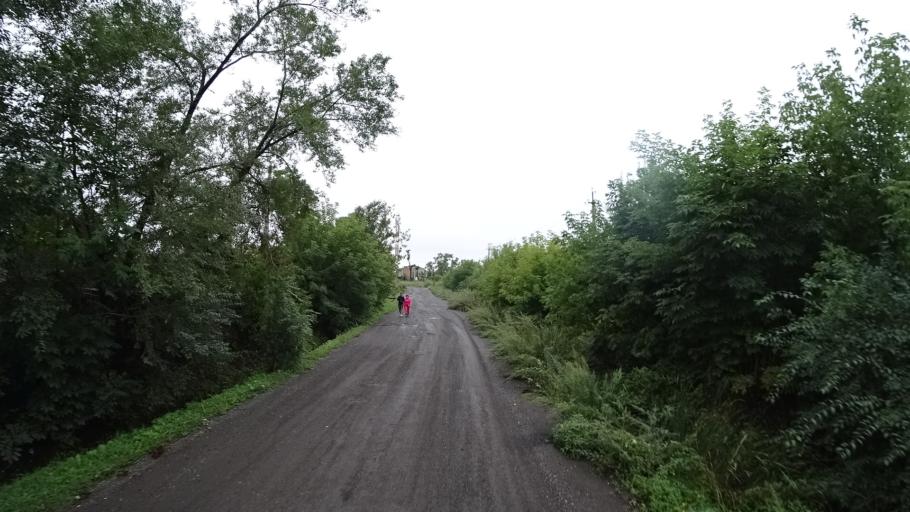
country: RU
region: Primorskiy
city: Monastyrishche
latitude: 44.2097
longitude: 132.4426
